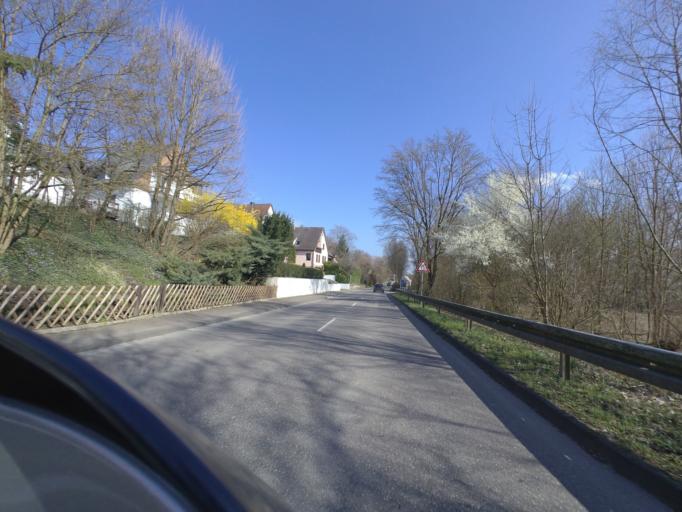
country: DE
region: Baden-Wuerttemberg
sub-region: Regierungsbezirk Stuttgart
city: Nurtingen
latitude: 48.6413
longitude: 9.3375
